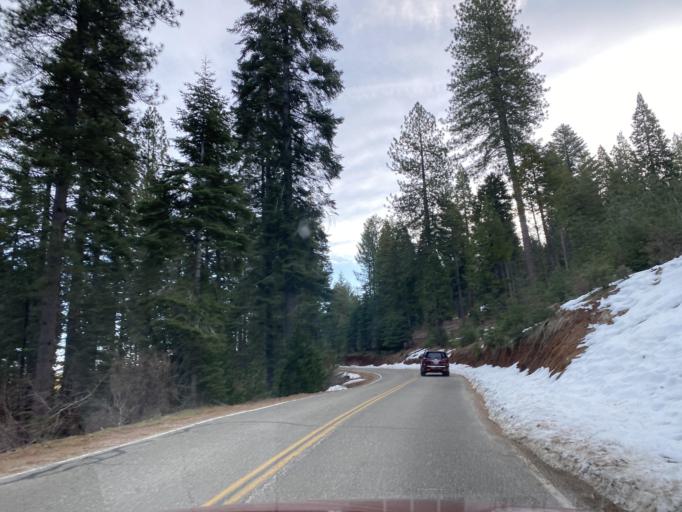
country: US
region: California
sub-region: Amador County
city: Pioneer
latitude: 38.5088
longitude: -120.5002
